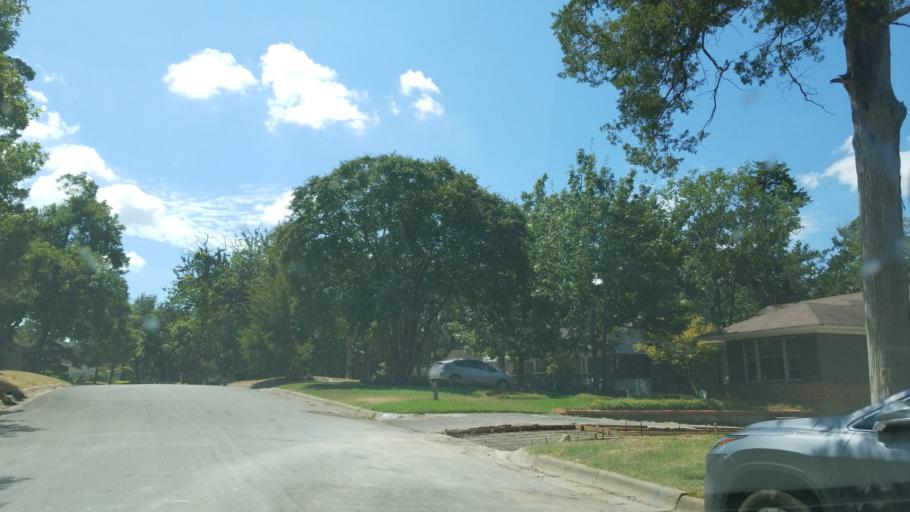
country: US
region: Texas
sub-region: Dallas County
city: Dallas
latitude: 32.7645
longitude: -96.8327
